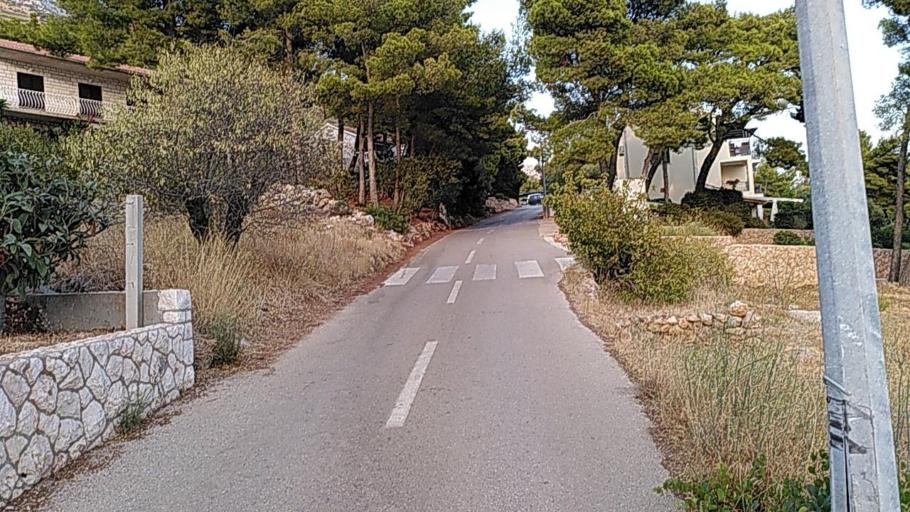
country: HR
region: Splitsko-Dalmatinska
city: Stari Grad
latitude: 43.1348
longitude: 16.5865
